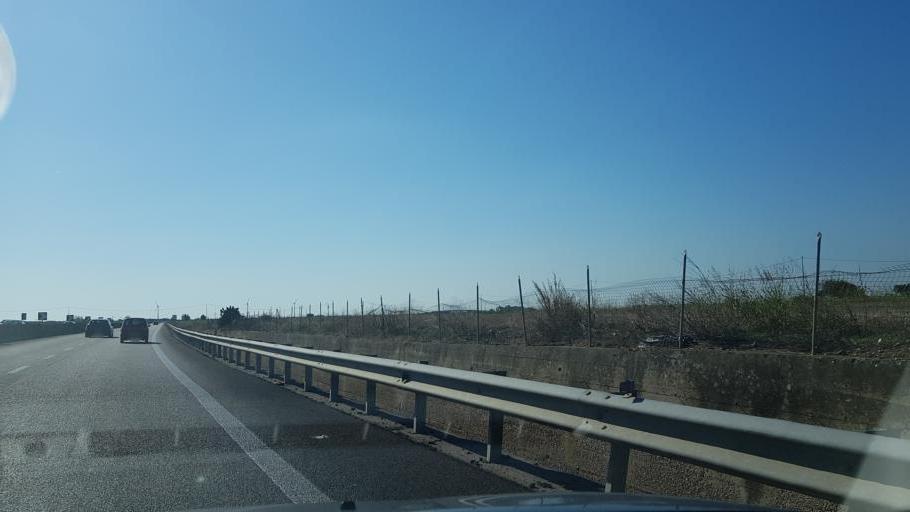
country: IT
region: Apulia
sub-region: Provincia di Brindisi
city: La Rosa
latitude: 40.5917
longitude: 17.9722
